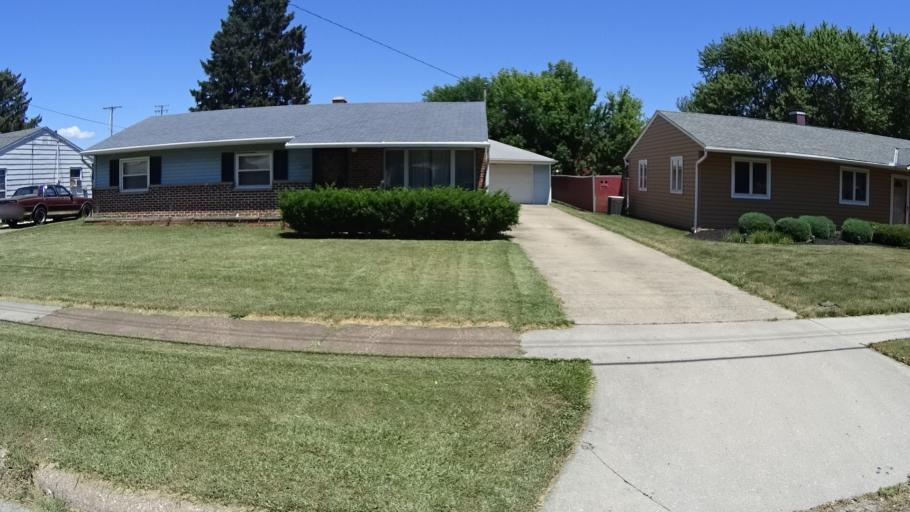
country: US
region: Ohio
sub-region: Erie County
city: Sandusky
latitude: 41.4407
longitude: -82.6841
